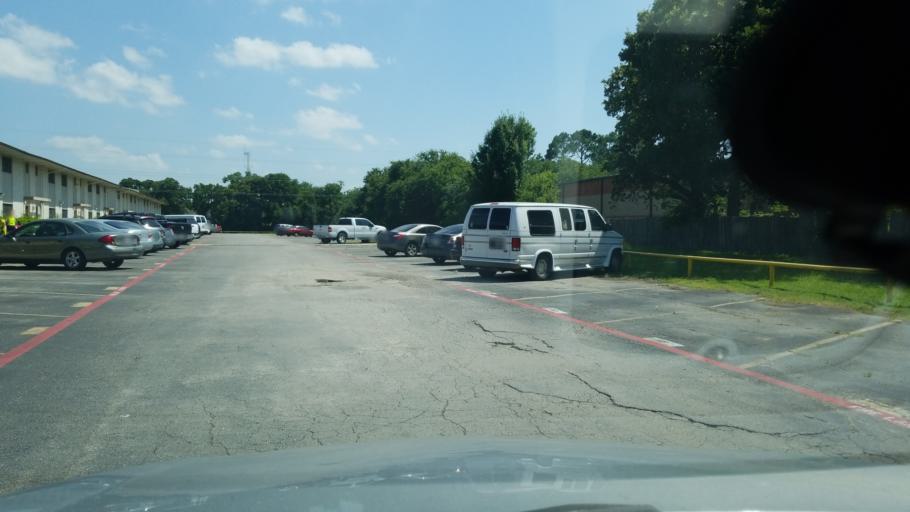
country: US
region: Texas
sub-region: Dallas County
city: Irving
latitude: 32.8189
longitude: -96.9554
